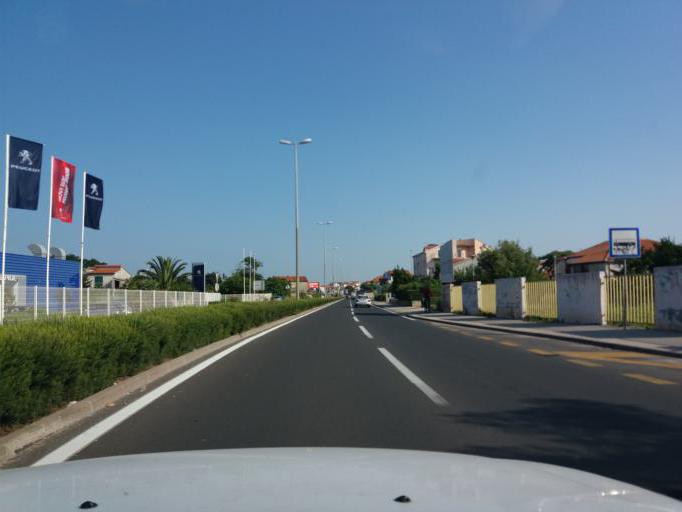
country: HR
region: Zadarska
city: Zadar
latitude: 44.1048
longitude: 15.2630
